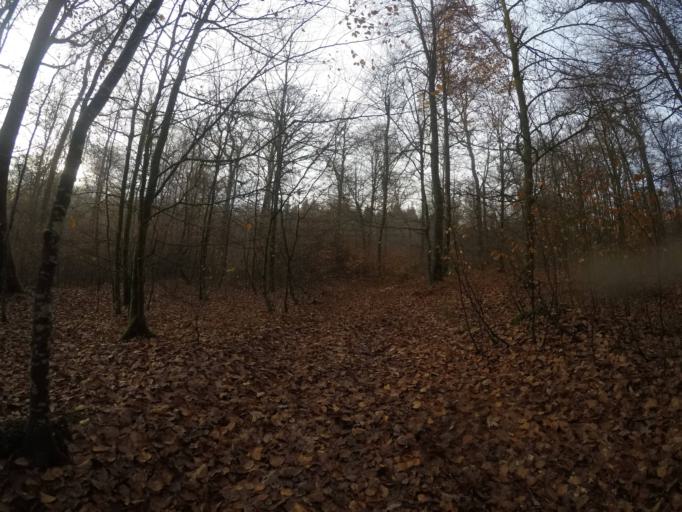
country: BE
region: Wallonia
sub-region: Province du Luxembourg
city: Habay-la-Vieille
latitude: 49.7611
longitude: 5.5986
